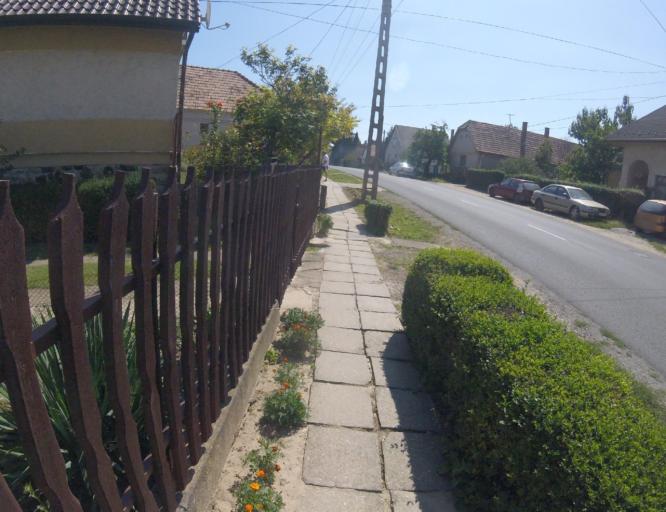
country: HU
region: Fejer
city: Pazmand
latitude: 47.2817
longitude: 18.6560
